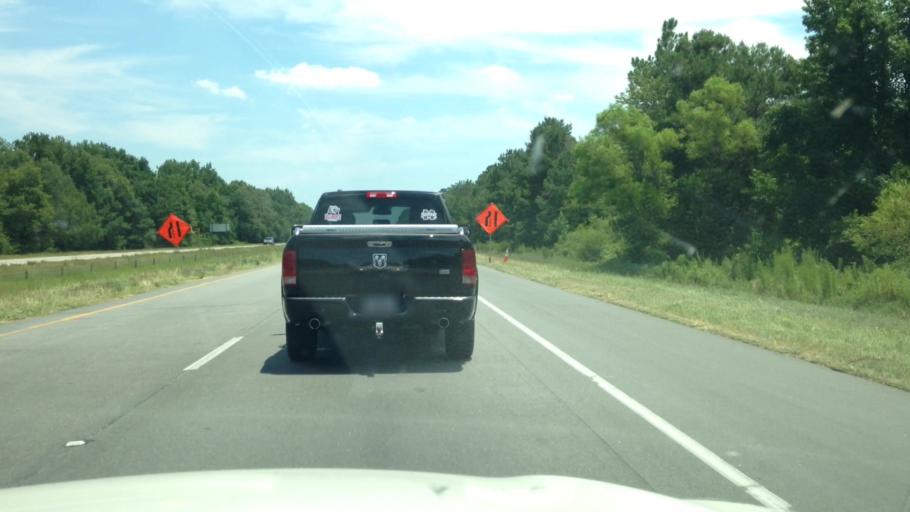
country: US
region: South Carolina
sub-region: Lee County
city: Bishopville
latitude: 34.1870
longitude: -80.2013
